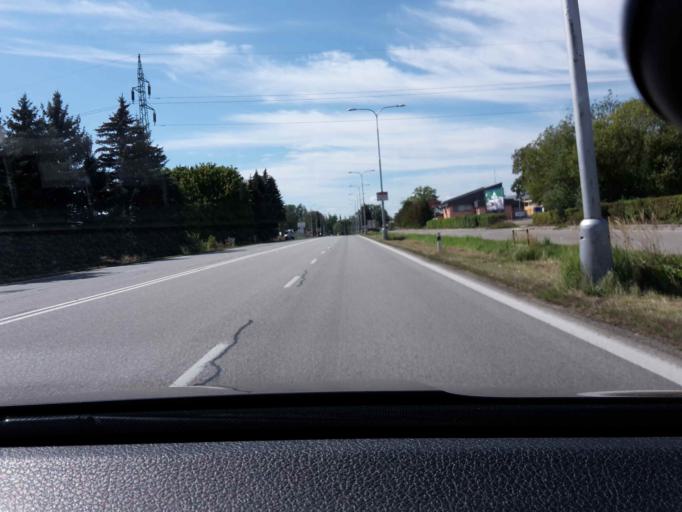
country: CZ
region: Jihocesky
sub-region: Okres Jindrichuv Hradec
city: Jindrichuv Hradec
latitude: 49.1576
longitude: 15.0206
